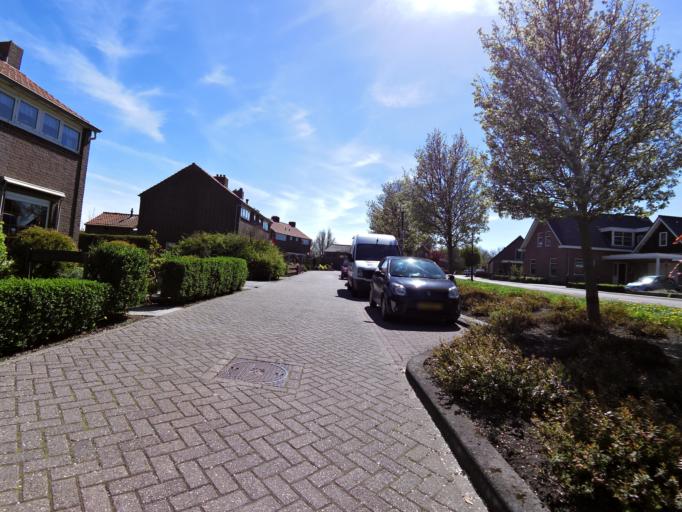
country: NL
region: South Holland
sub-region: Gemeente Brielle
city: Brielle
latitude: 51.8880
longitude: 4.1381
